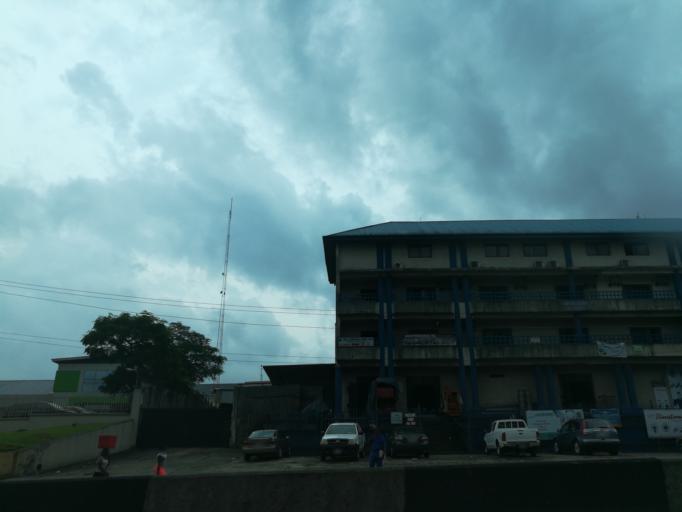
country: NG
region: Rivers
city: Port Harcourt
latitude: 4.8419
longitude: 7.0343
